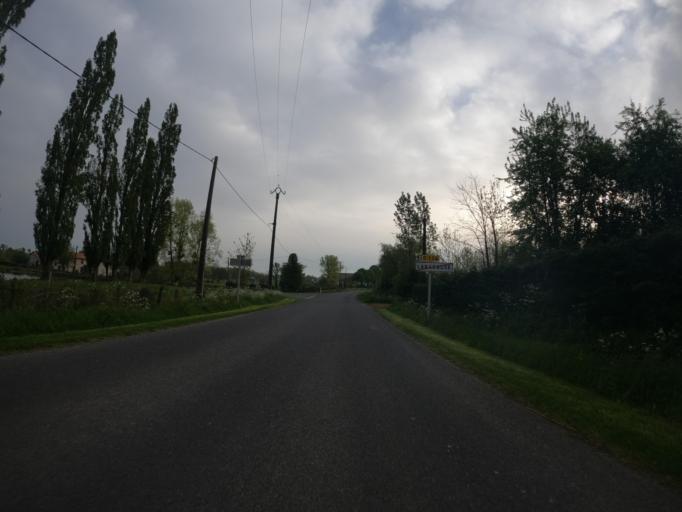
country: FR
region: Poitou-Charentes
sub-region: Departement des Deux-Sevres
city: La Chapelle-Saint-Laurent
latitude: 46.6967
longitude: -0.4951
